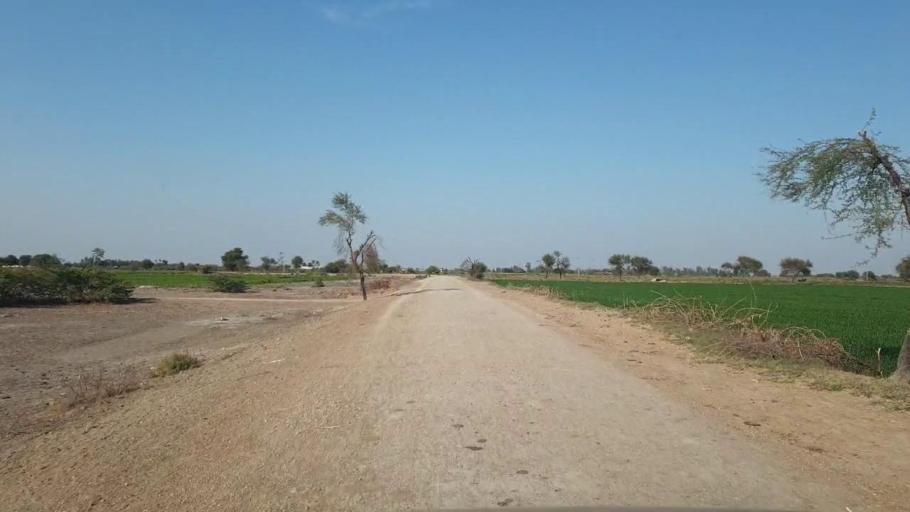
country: PK
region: Sindh
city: Shahpur Chakar
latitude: 26.1670
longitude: 68.6819
